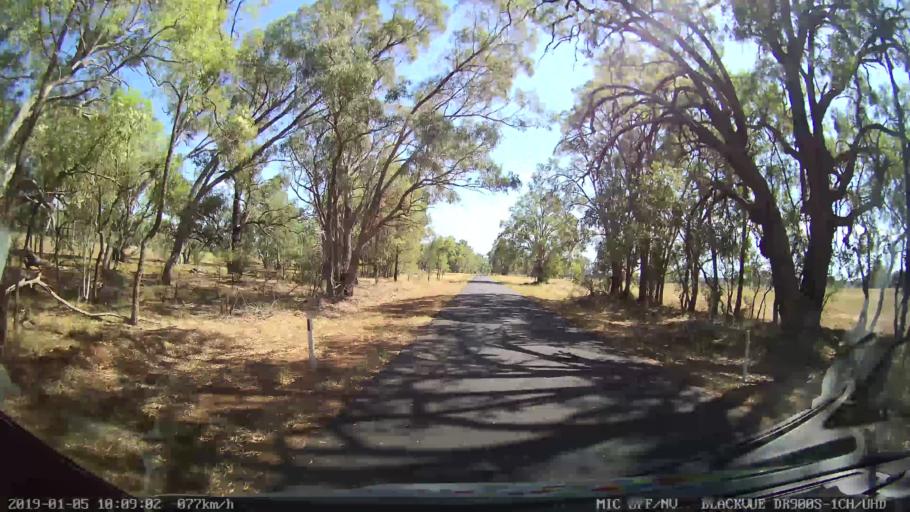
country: AU
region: New South Wales
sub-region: Gilgandra
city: Gilgandra
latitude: -31.6353
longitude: 148.8839
